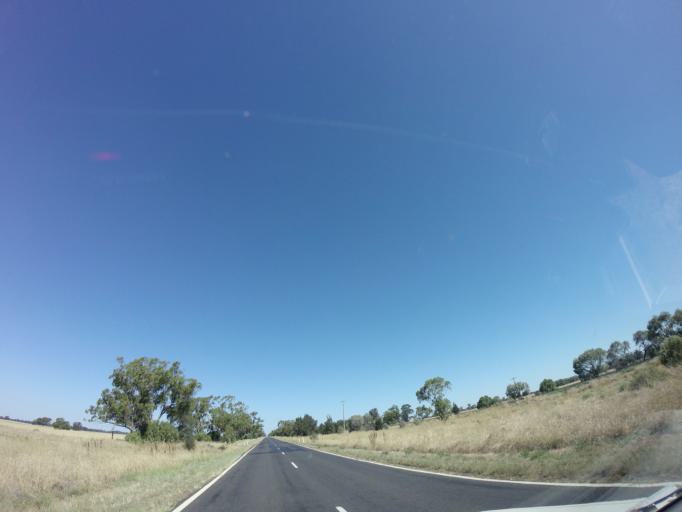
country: AU
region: New South Wales
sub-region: Bogan
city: Nyngan
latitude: -31.8040
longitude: 147.6533
